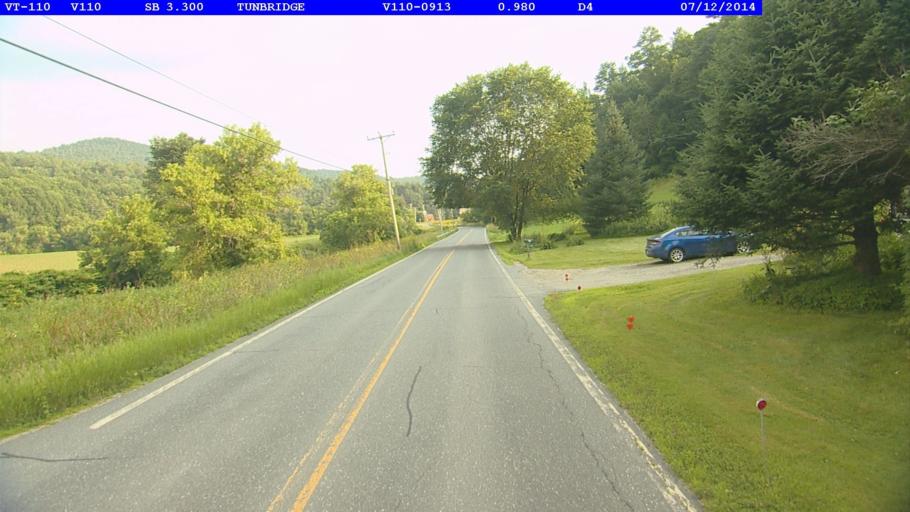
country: US
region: Vermont
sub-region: Orange County
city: Chelsea
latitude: 43.8649
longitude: -72.4994
